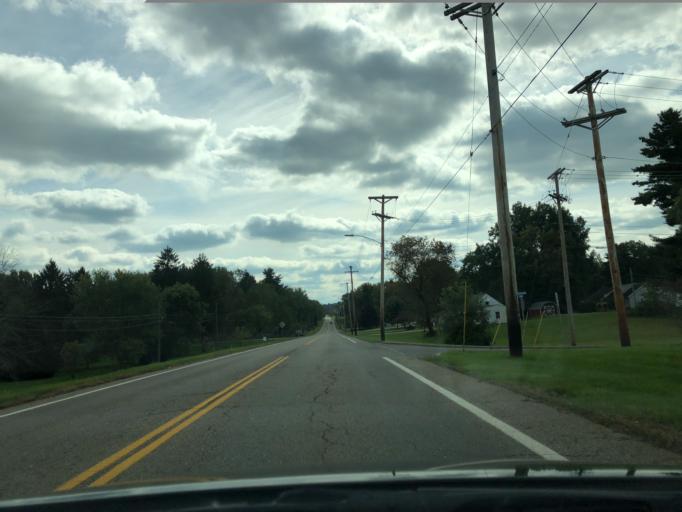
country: US
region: Ohio
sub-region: Stark County
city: Brewster
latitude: 40.7052
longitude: -81.5981
